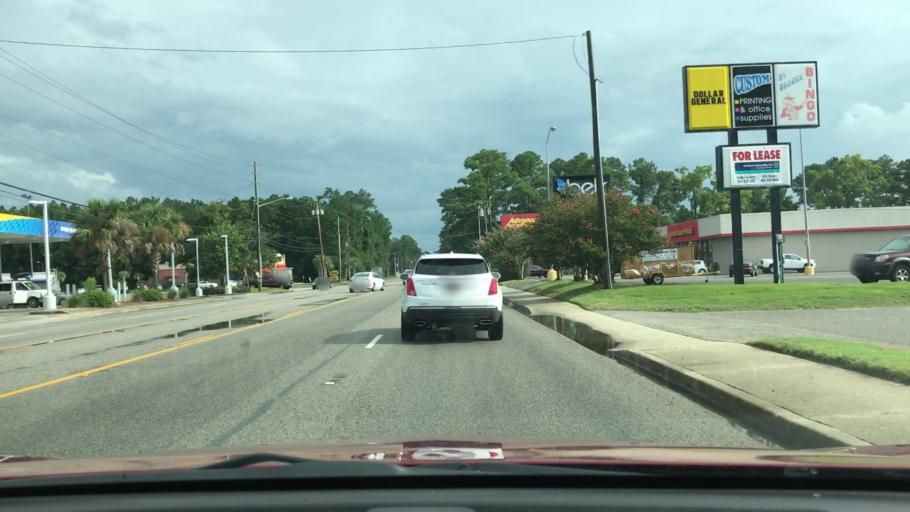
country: US
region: South Carolina
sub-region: Georgetown County
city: Georgetown
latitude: 33.3909
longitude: -79.2890
